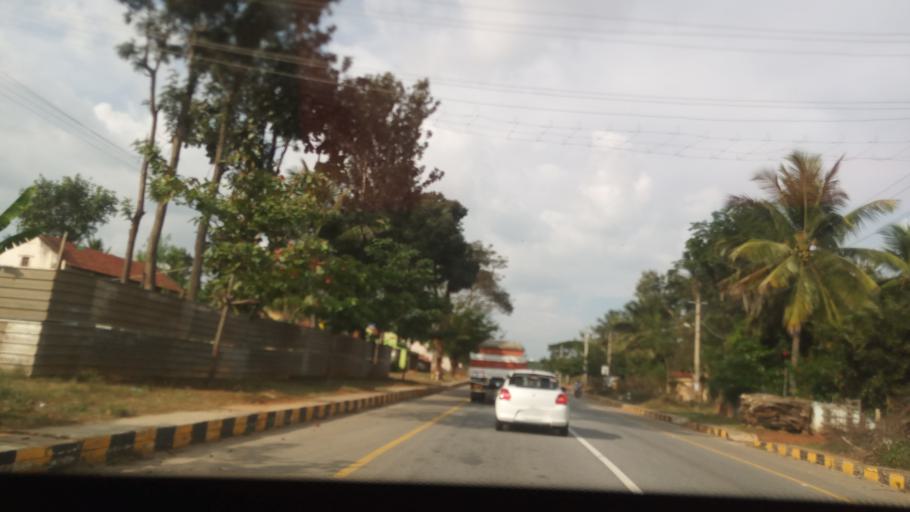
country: IN
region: Karnataka
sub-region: Tumkur
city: Kunigal
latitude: 12.8661
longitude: 77.0402
